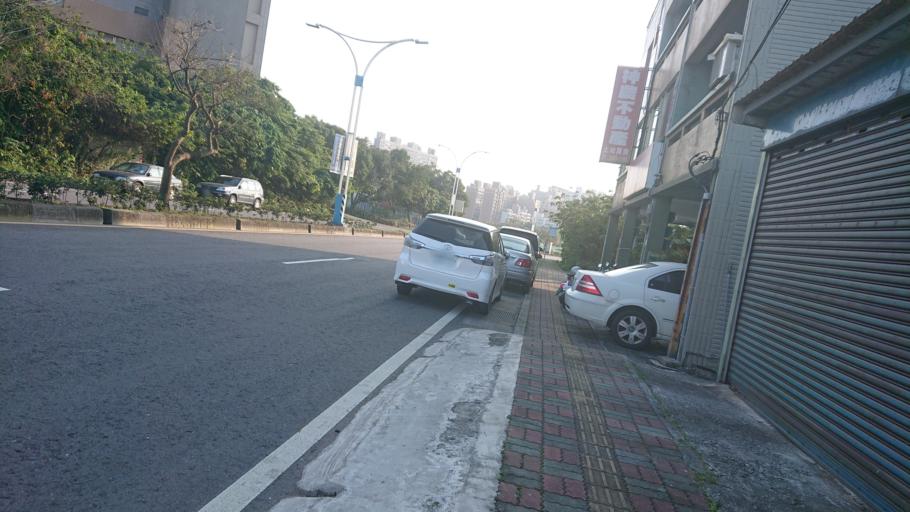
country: TW
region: Taipei
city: Taipei
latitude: 25.1894
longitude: 121.4263
